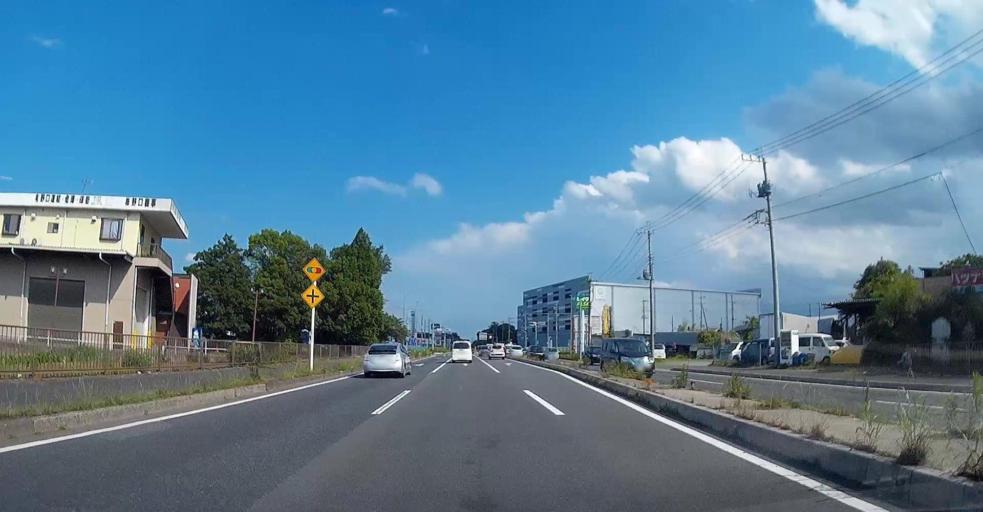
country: JP
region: Chiba
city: Noda
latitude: 35.9917
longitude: 139.8504
